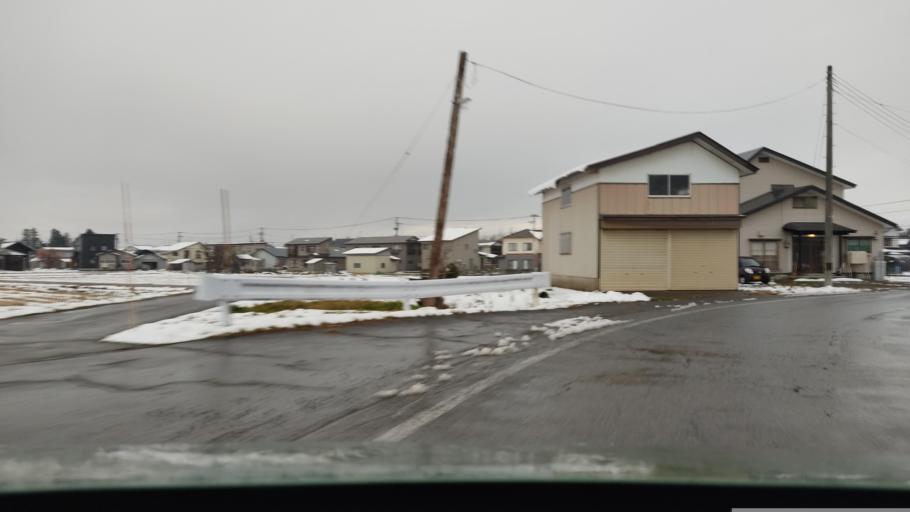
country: JP
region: Akita
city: Omagari
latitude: 39.4550
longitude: 140.5274
